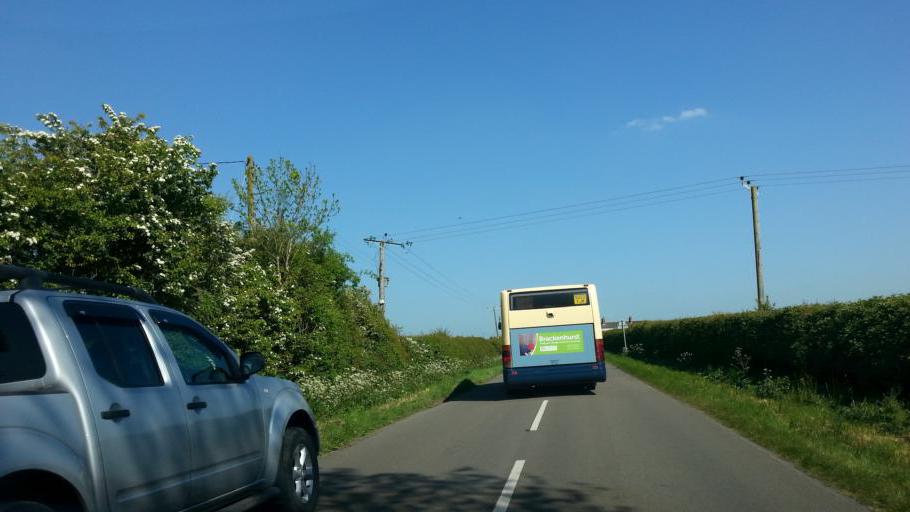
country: GB
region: England
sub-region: Nottinghamshire
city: Farndon
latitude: 53.0077
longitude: -0.8162
